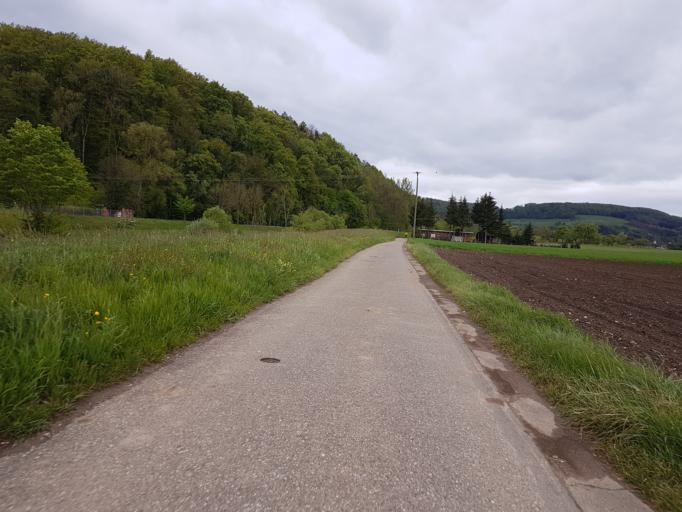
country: DE
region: Baden-Wuerttemberg
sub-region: Freiburg Region
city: Lauchringen
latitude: 47.6331
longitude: 8.3434
